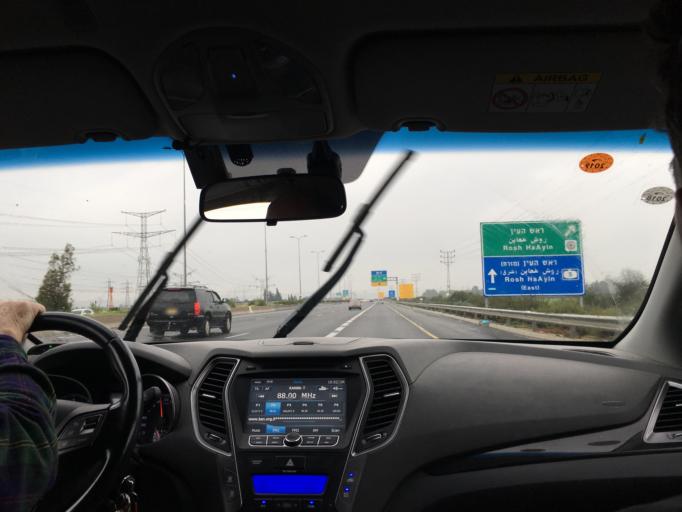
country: IL
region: Central District
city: Petah Tiqwa
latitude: 32.1183
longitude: 34.9179
